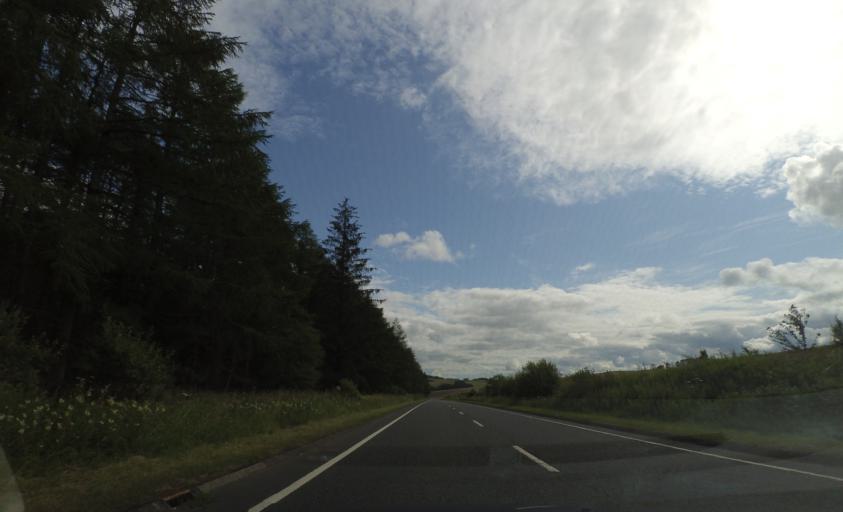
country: GB
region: Scotland
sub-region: The Scottish Borders
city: Selkirk
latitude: 55.5180
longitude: -2.8405
